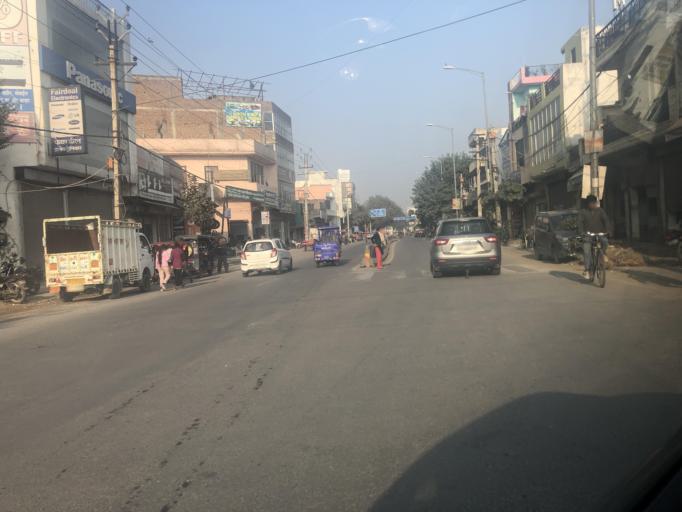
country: IN
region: Haryana
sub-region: Jhajjar
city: Bahadurgarh
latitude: 28.6155
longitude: 76.9823
